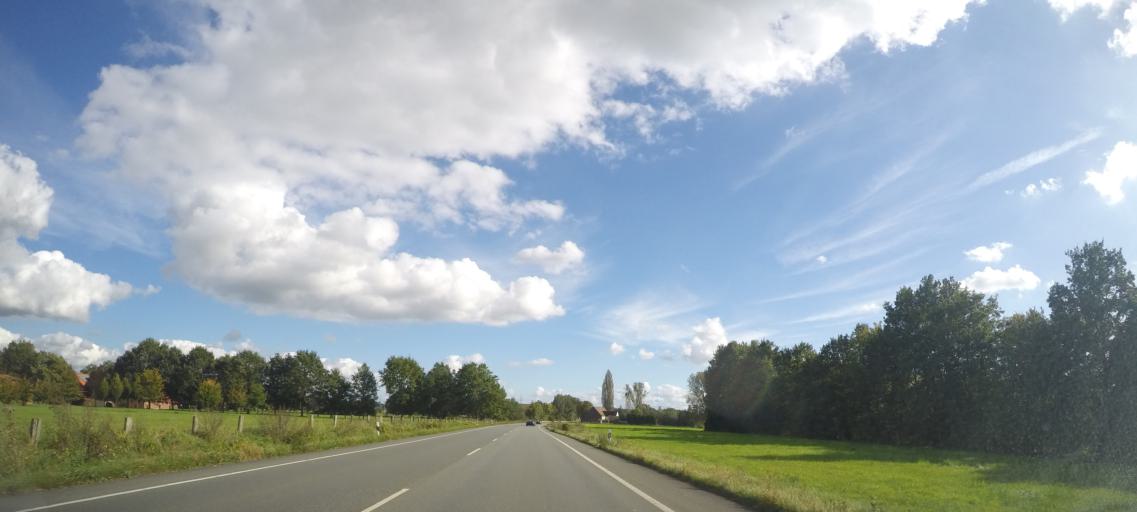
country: DE
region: North Rhine-Westphalia
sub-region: Regierungsbezirk Arnsberg
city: Welver
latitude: 51.6836
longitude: 7.9950
